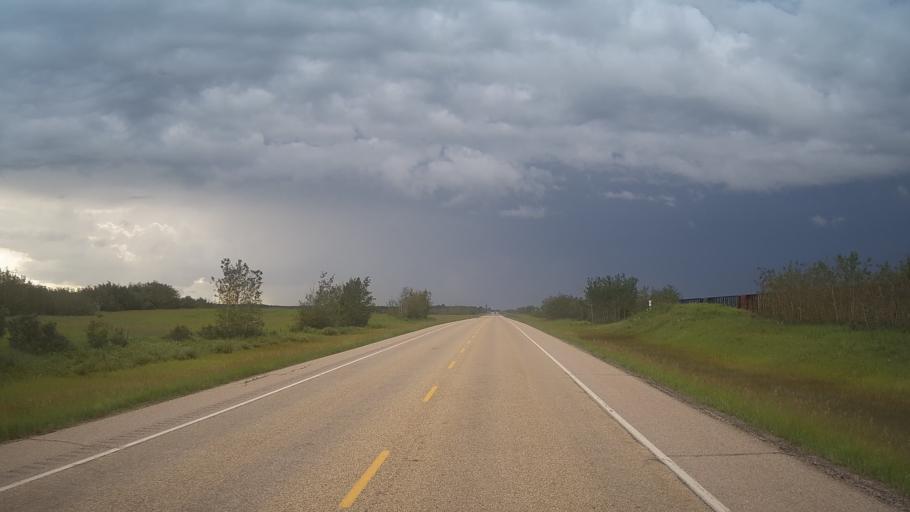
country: CA
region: Alberta
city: Tofield
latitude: 53.2739
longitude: -112.3837
